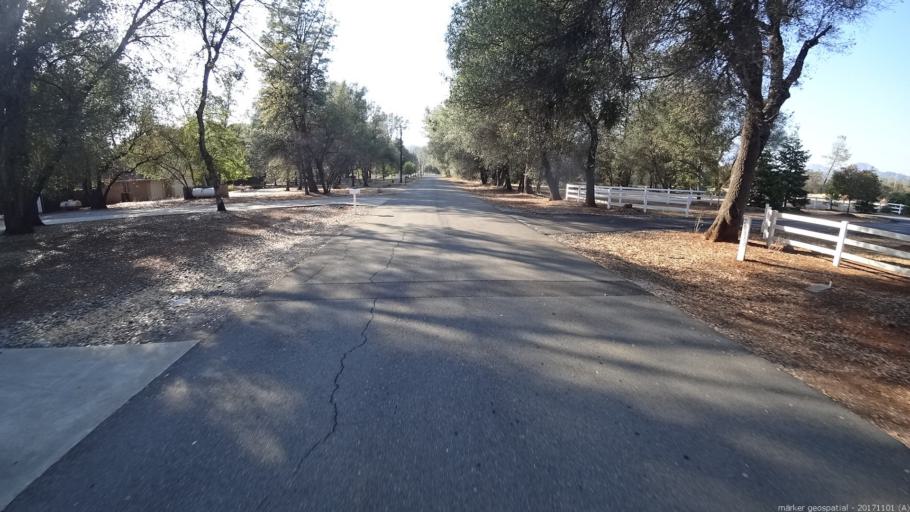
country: US
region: California
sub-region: Shasta County
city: Bella Vista
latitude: 40.6806
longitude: -122.2949
